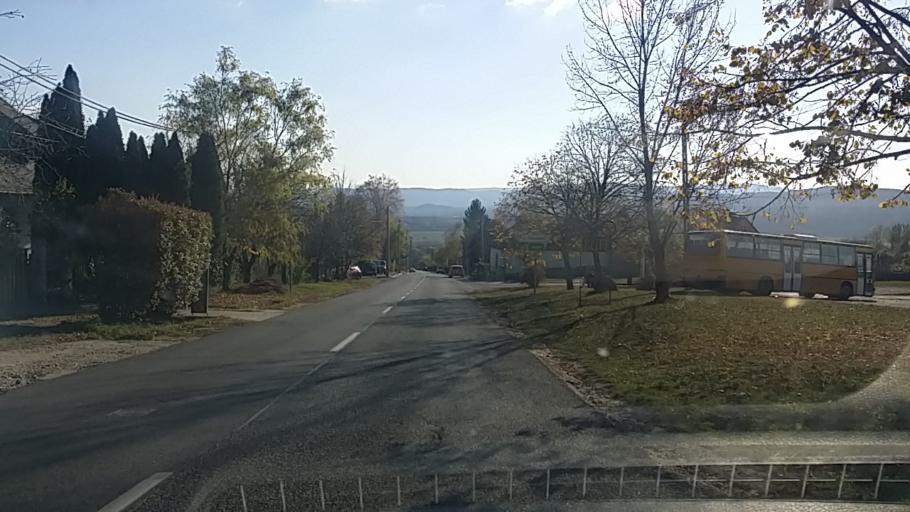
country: HU
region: Pest
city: Pilisszanto
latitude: 47.6750
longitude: 18.8860
